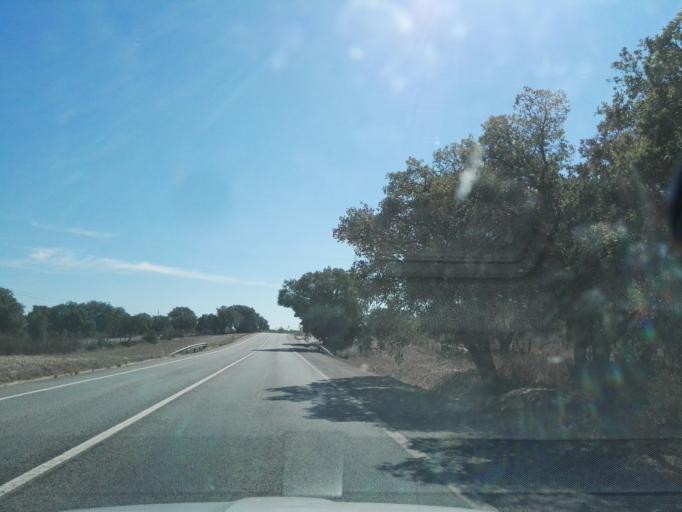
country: PT
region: Santarem
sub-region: Benavente
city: Poceirao
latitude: 38.8584
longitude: -8.7786
